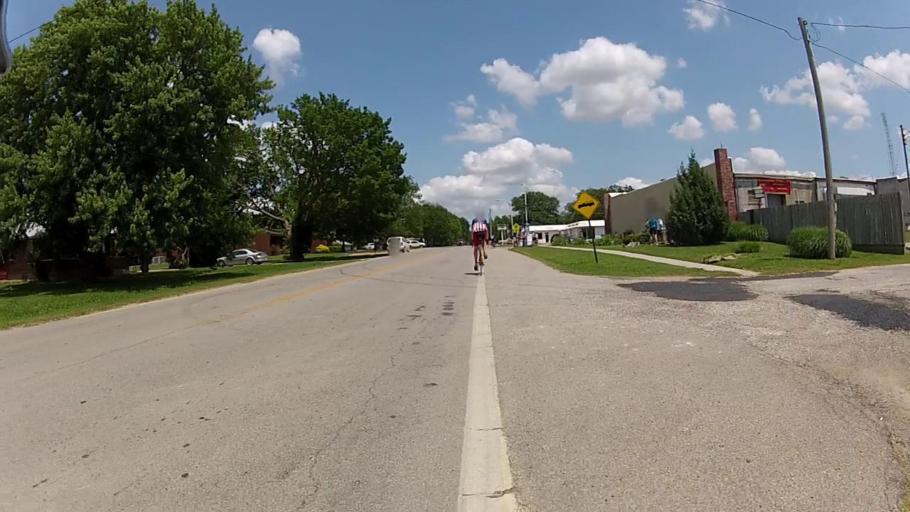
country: US
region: Kansas
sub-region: Labette County
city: Altamont
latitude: 37.1930
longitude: -95.2978
